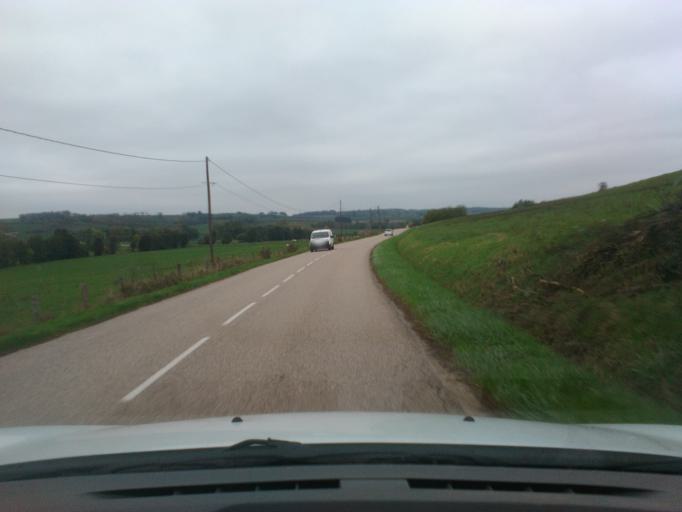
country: FR
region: Lorraine
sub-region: Departement des Vosges
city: Vincey
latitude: 48.3019
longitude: 6.2884
